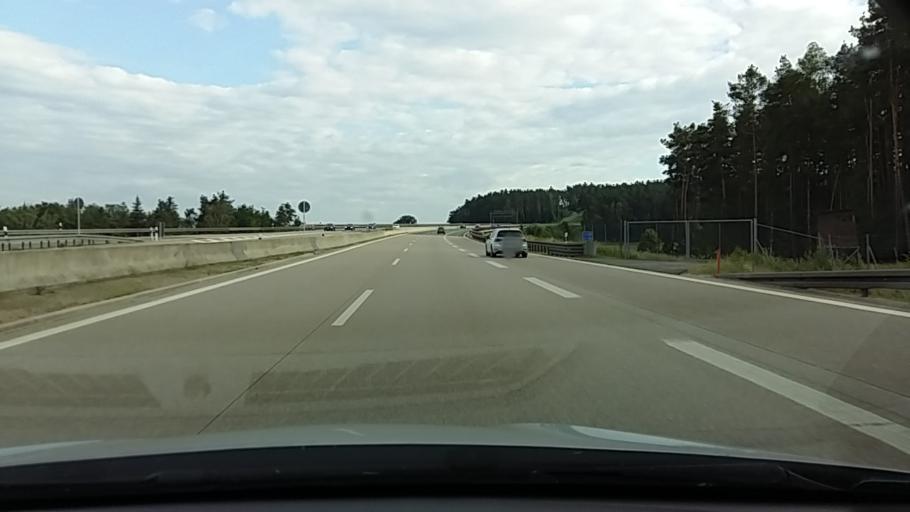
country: DE
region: Bavaria
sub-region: Upper Palatinate
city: Wernberg-Koblitz
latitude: 49.5138
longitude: 12.1622
